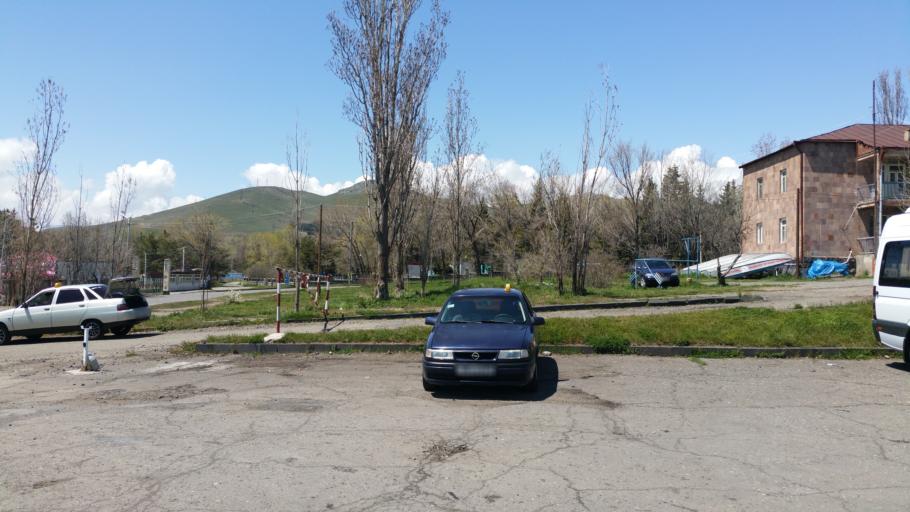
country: AM
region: Geghark'unik'i Marz
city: Sevan
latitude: 40.5638
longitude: 45.0082
